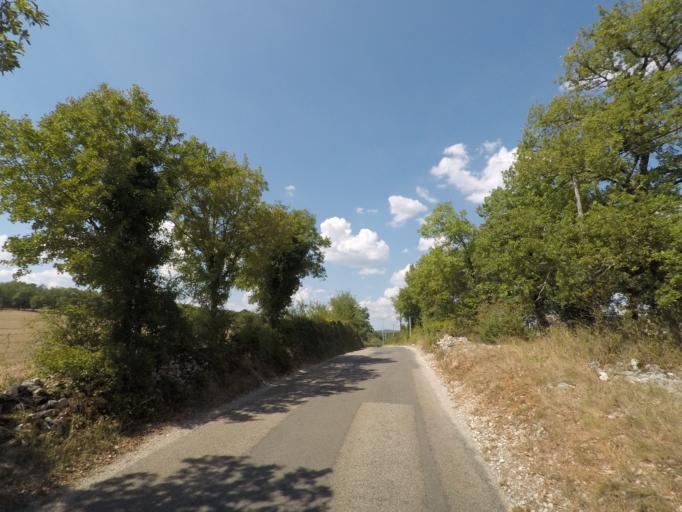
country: FR
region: Midi-Pyrenees
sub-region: Departement du Lot
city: Lalbenque
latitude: 44.5166
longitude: 1.6314
